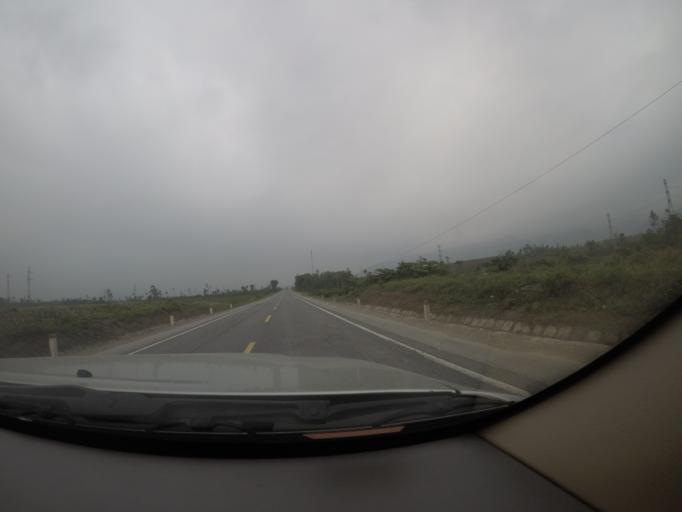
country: VN
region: Ha Tinh
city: Ky Anh
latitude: 18.0364
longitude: 106.3071
